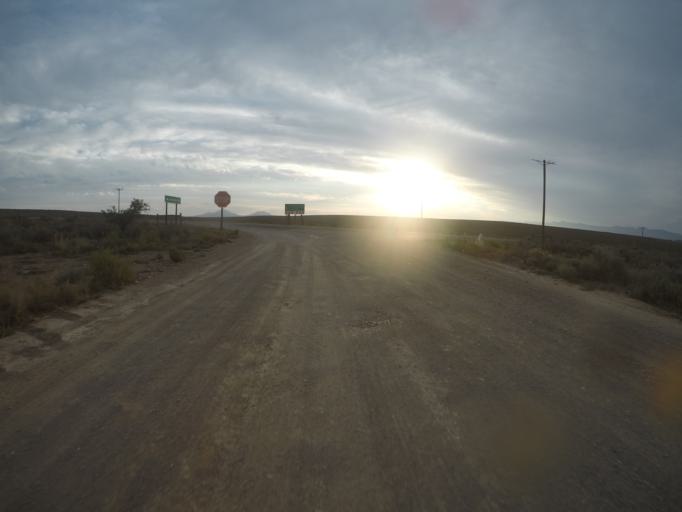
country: ZA
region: Eastern Cape
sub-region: Cacadu District Municipality
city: Willowmore
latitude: -33.5759
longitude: 23.1681
